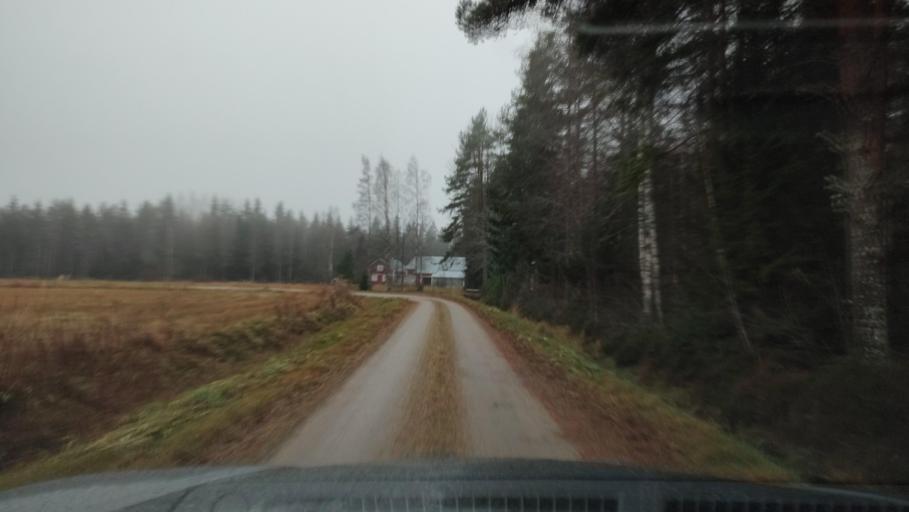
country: FI
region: Southern Ostrobothnia
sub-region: Suupohja
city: Karijoki
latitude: 62.1875
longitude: 21.7707
